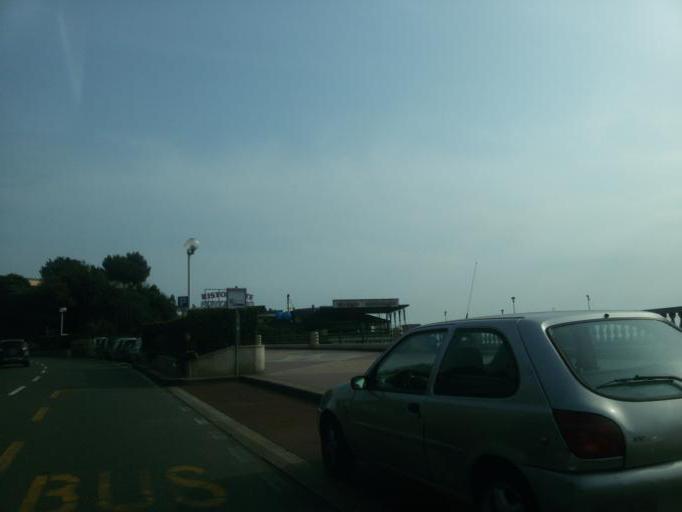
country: IT
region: Liguria
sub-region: Provincia di Genova
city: San Teodoro
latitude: 44.3933
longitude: 8.9511
